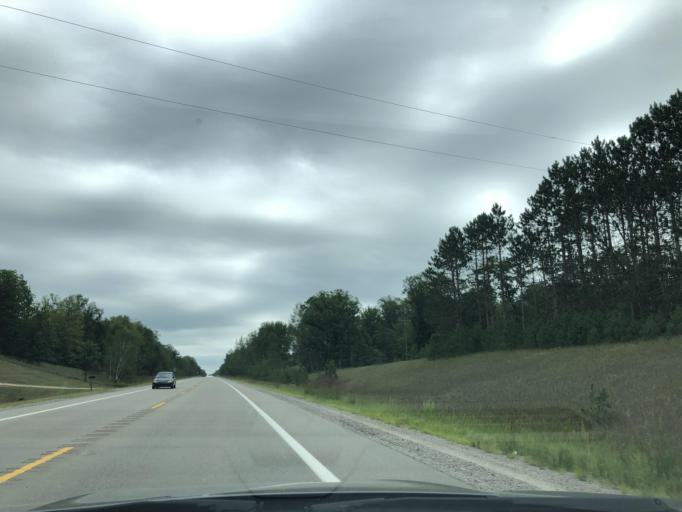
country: US
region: Michigan
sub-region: Clare County
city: Harrison
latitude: 44.0313
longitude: -85.0147
